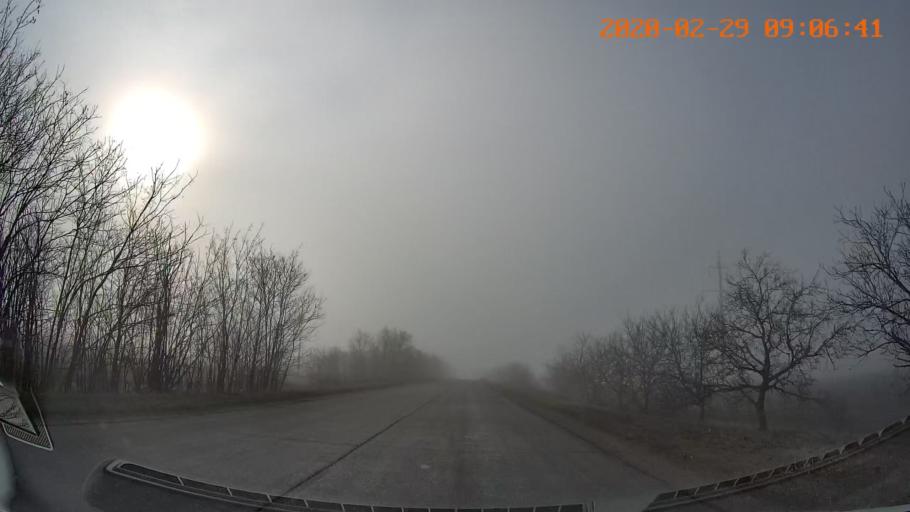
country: MD
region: Telenesti
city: Tiraspolul Nou
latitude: 46.8724
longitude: 29.7456
